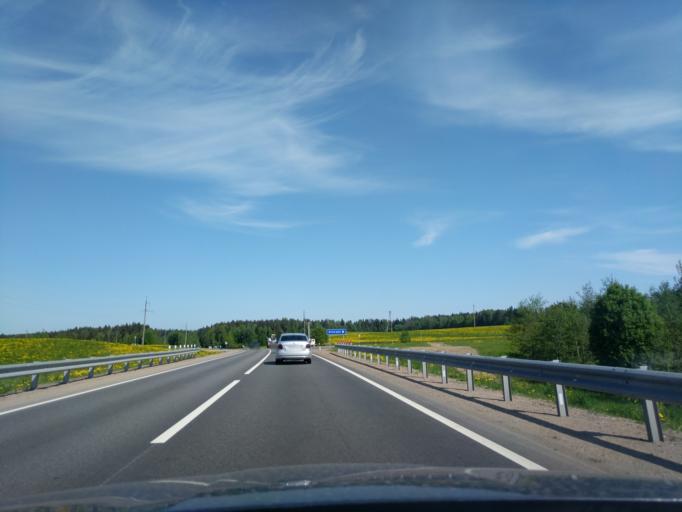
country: BY
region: Minsk
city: Bal'shavik
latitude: 54.0981
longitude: 27.5349
